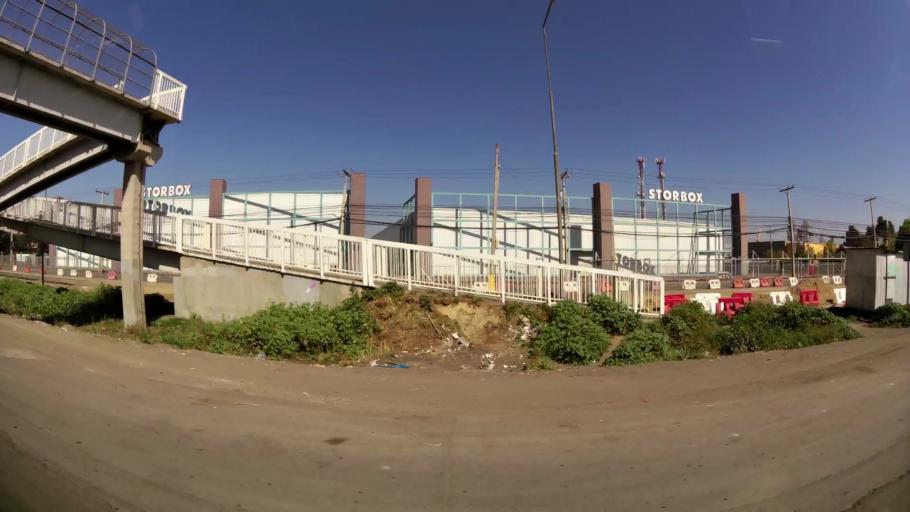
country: CL
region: Santiago Metropolitan
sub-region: Provincia de Chacabuco
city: Chicureo Abajo
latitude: -33.2963
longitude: -70.7319
